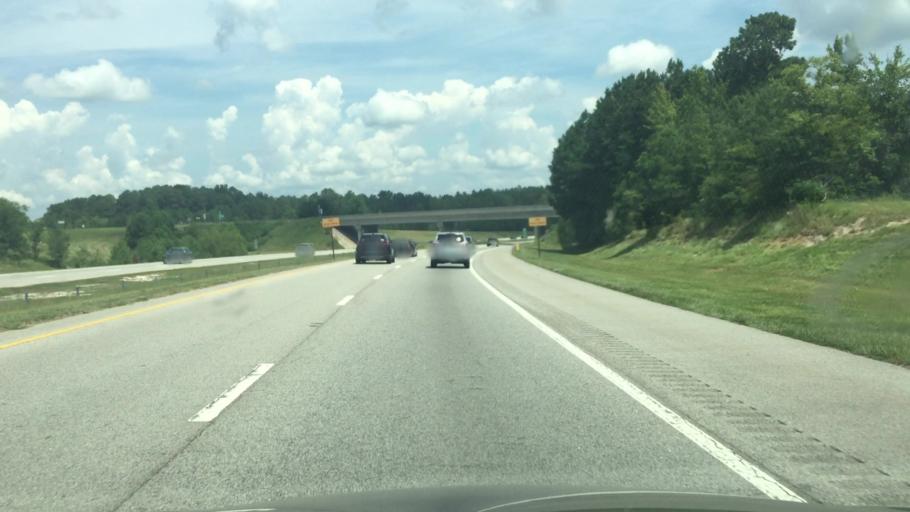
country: US
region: North Carolina
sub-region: Richmond County
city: Ellerbe
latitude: 35.0415
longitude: -79.7681
